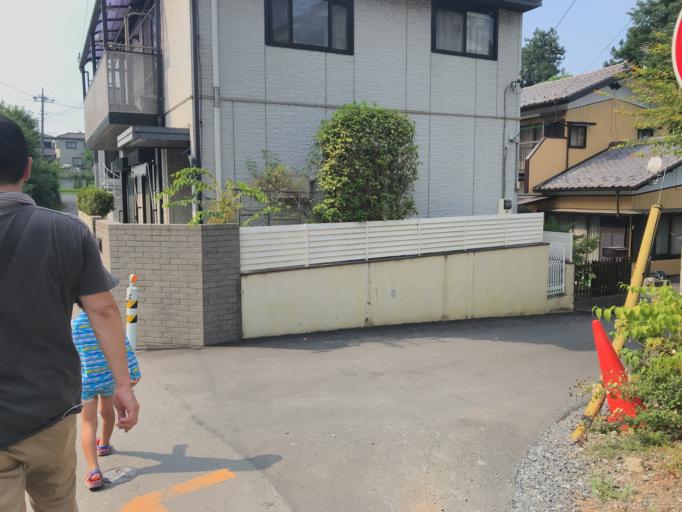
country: JP
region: Saitama
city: Chichibu
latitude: 35.9842
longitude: 139.1010
